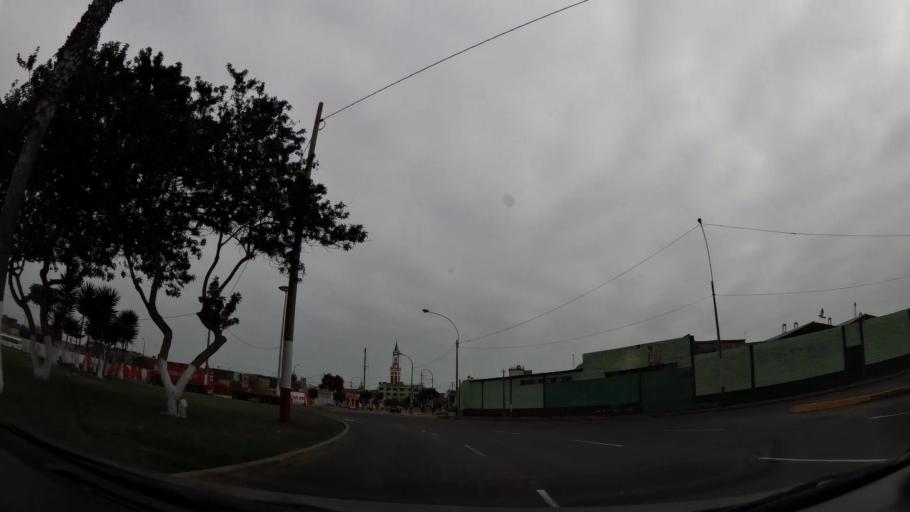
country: PE
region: Callao
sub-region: Callao
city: Callao
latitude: -12.0520
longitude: -77.1397
